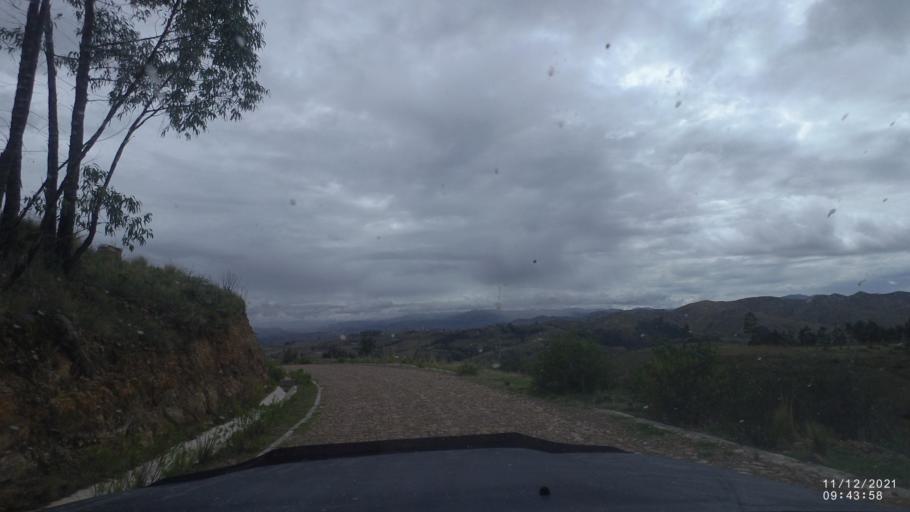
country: BO
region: Cochabamba
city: Tarata
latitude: -17.7998
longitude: -65.9753
